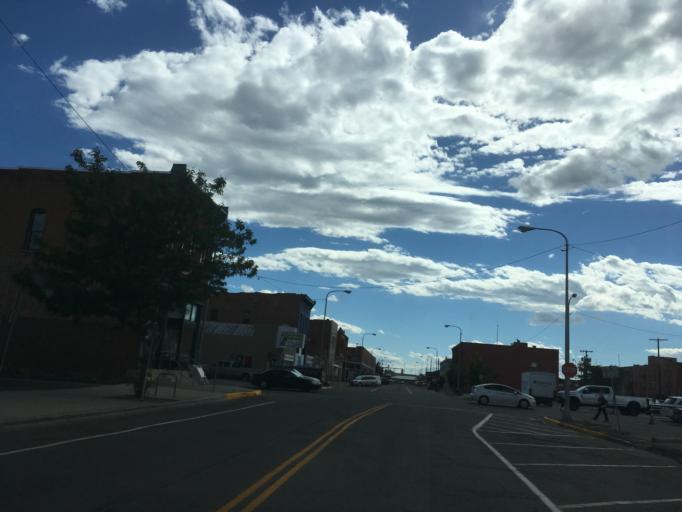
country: US
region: Montana
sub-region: Yellowstone County
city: Billings
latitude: 45.7813
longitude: -108.5023
